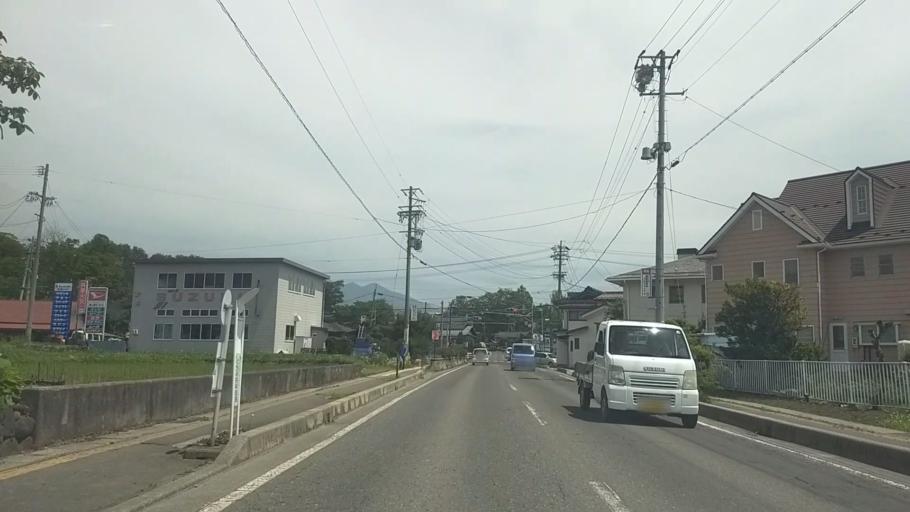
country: JP
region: Nagano
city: Chino
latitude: 35.9984
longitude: 138.1694
